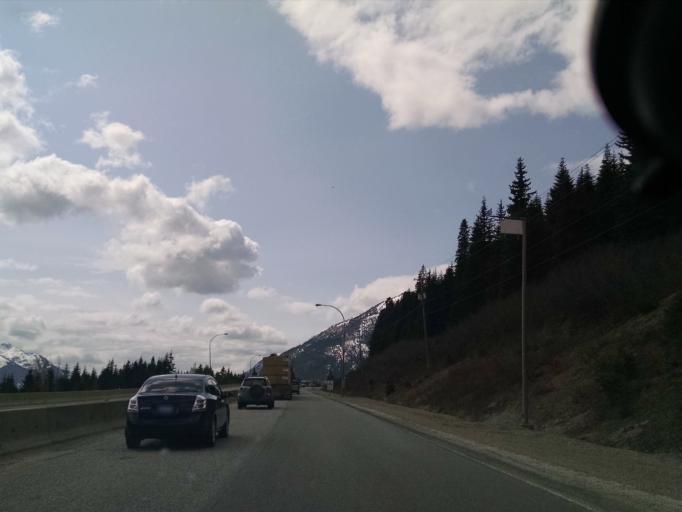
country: CA
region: British Columbia
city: Hope
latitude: 49.6041
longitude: -121.0656
